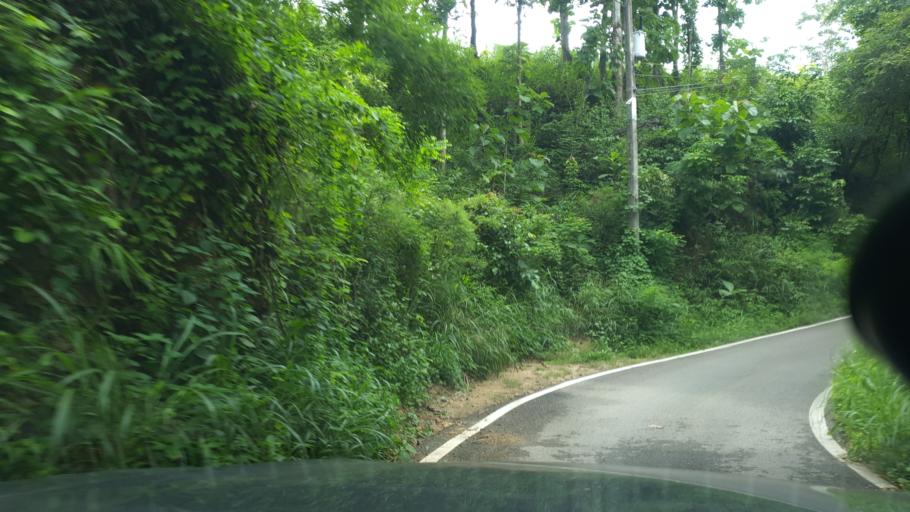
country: TH
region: Lamphun
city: Mae Tha
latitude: 18.5071
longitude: 99.2646
